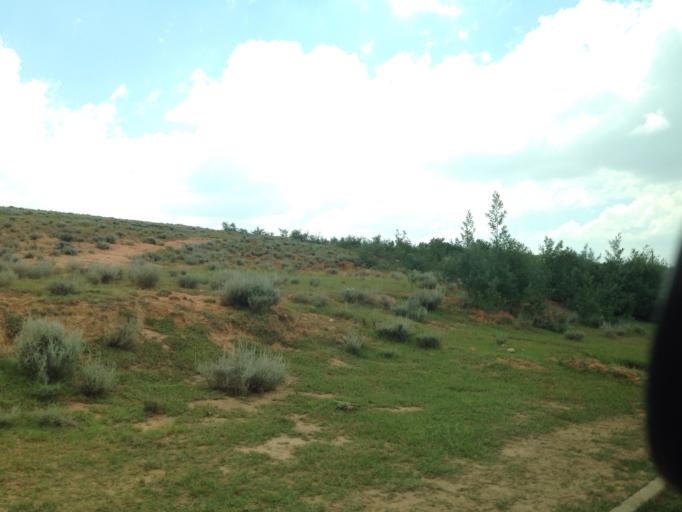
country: LS
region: Maseru
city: Maseru
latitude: -29.4562
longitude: 27.5641
